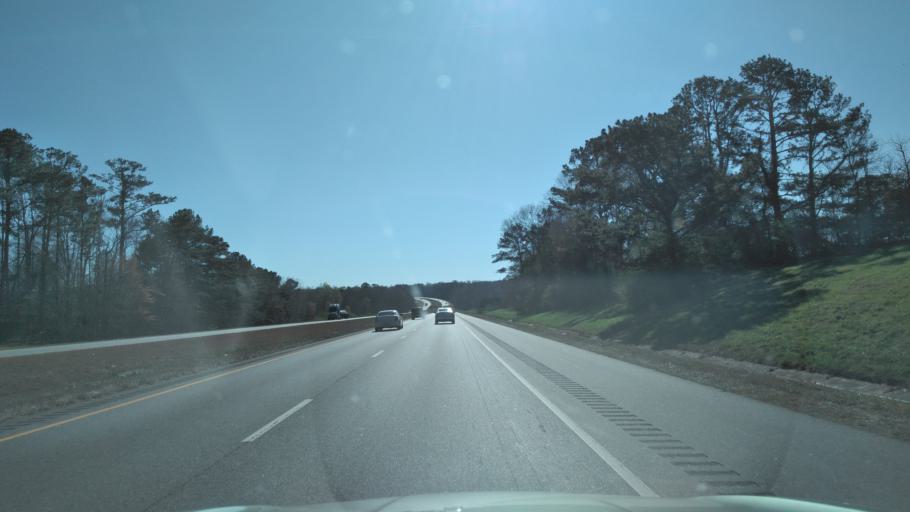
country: US
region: Alabama
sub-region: Lowndes County
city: Fort Deposit
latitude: 31.9508
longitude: -86.5531
